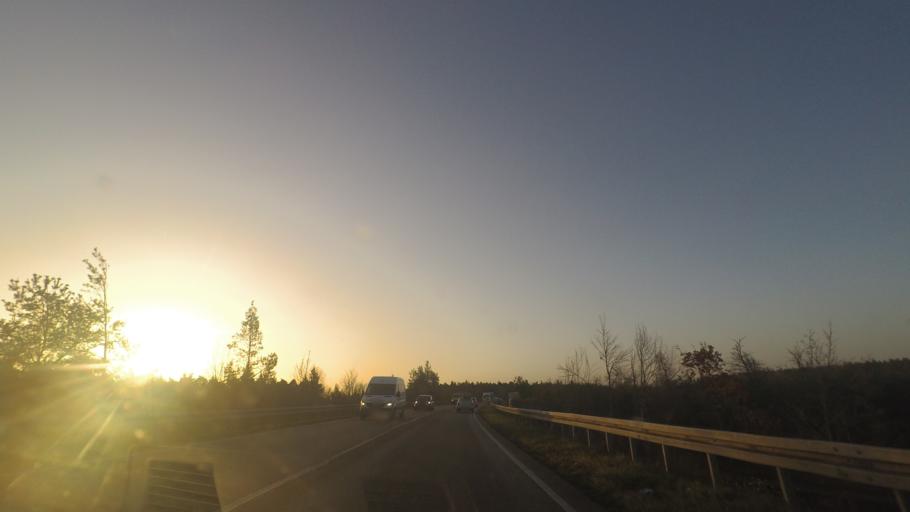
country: DE
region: Baden-Wuerttemberg
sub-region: Karlsruhe Region
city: Hambrucken
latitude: 49.1985
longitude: 8.5100
